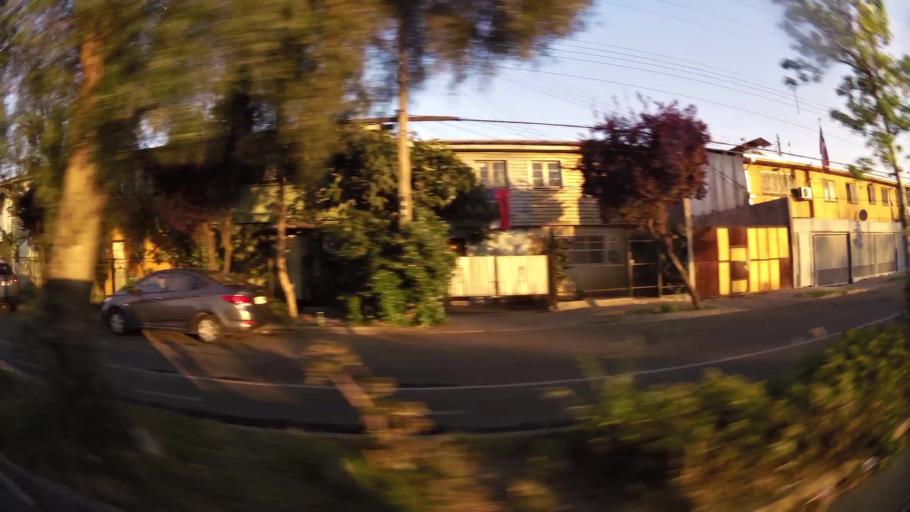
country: CL
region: Santiago Metropolitan
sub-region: Provincia de Santiago
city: Santiago
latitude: -33.4725
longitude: -70.6833
